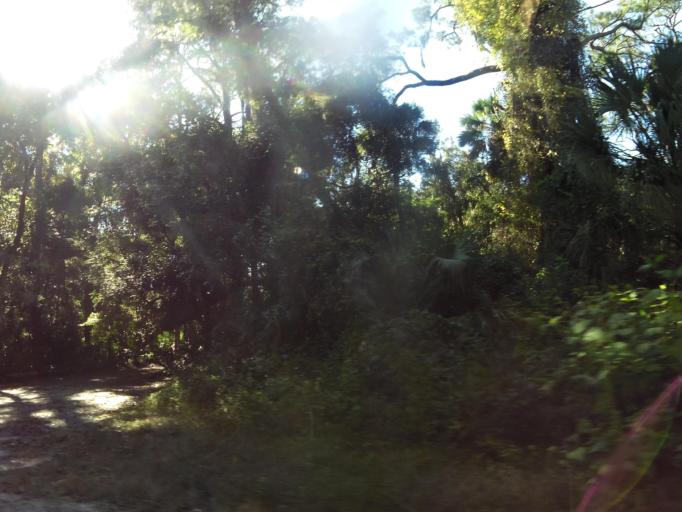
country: US
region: Florida
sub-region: Duval County
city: Atlantic Beach
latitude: 30.4149
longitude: -81.4324
